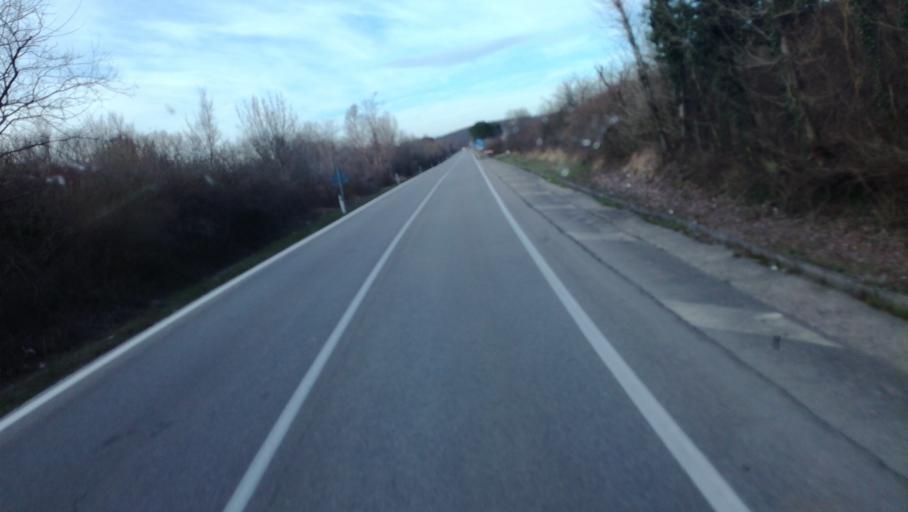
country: IT
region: Tuscany
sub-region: Provincia di Siena
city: Rosia
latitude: 43.2010
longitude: 11.2763
